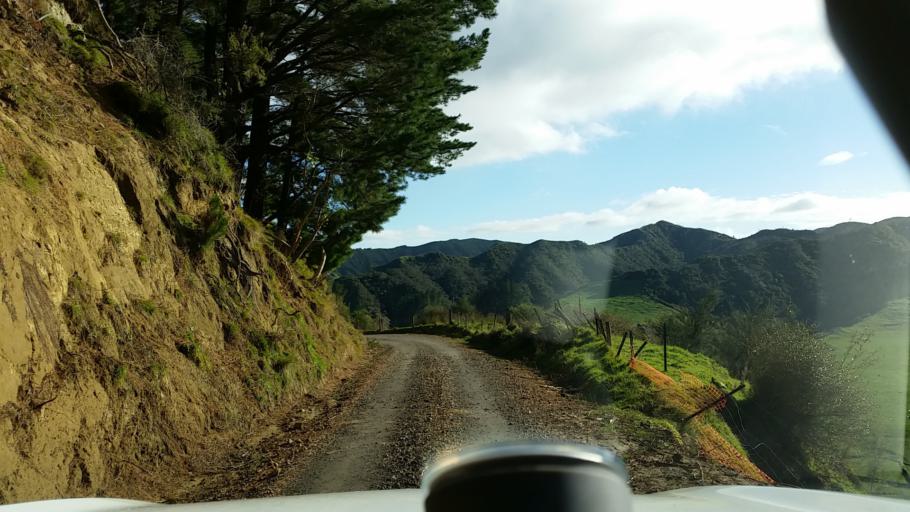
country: NZ
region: Taranaki
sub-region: South Taranaki District
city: Eltham
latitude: -39.4093
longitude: 174.5357
